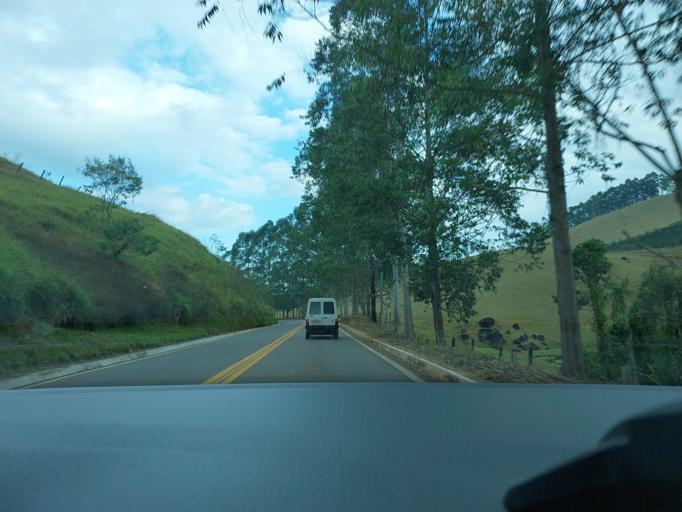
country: BR
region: Minas Gerais
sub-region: Mirai
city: Mirai
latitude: -21.0285
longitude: -42.5393
